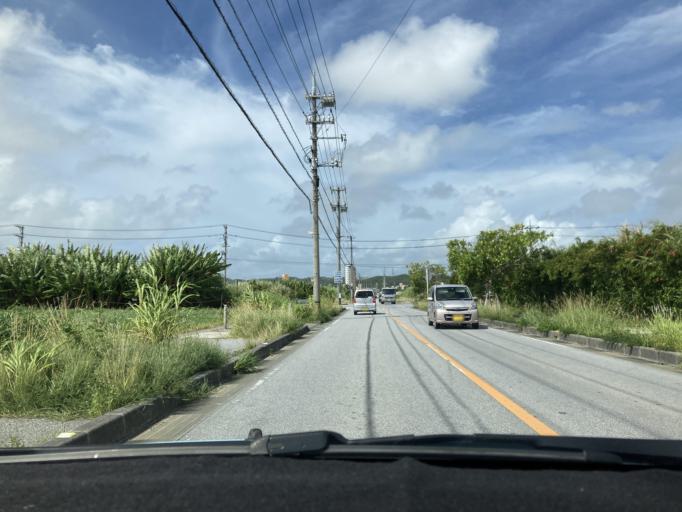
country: JP
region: Okinawa
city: Ginowan
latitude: 26.2214
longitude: 127.7739
